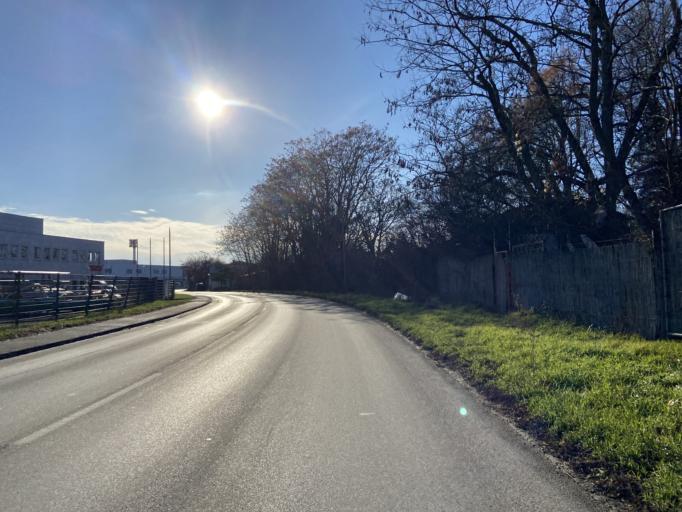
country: AT
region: Lower Austria
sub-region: Politischer Bezirk Modling
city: Neu-Guntramsdorf
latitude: 48.0647
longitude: 16.3255
